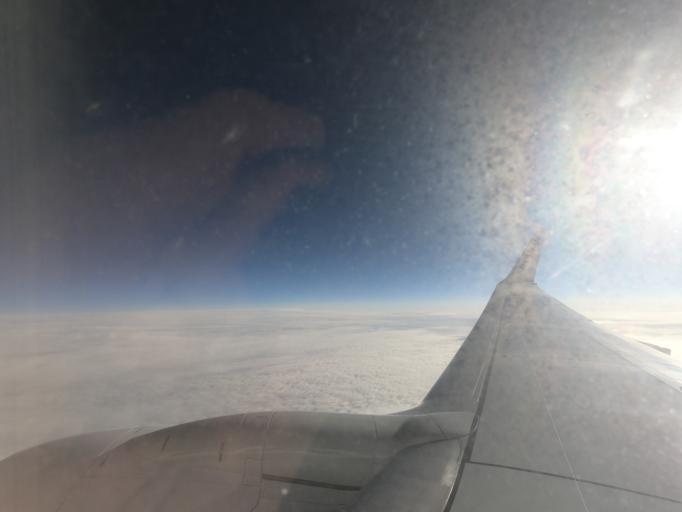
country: BE
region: Flanders
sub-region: Provincie Antwerpen
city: Puurs
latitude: 51.0466
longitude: 4.2714
